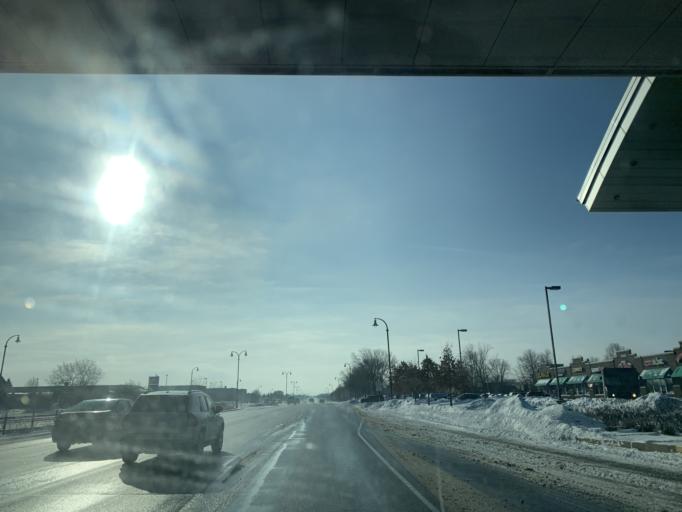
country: US
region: Minnesota
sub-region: Dakota County
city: Apple Valley
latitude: 44.7258
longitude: -93.2179
